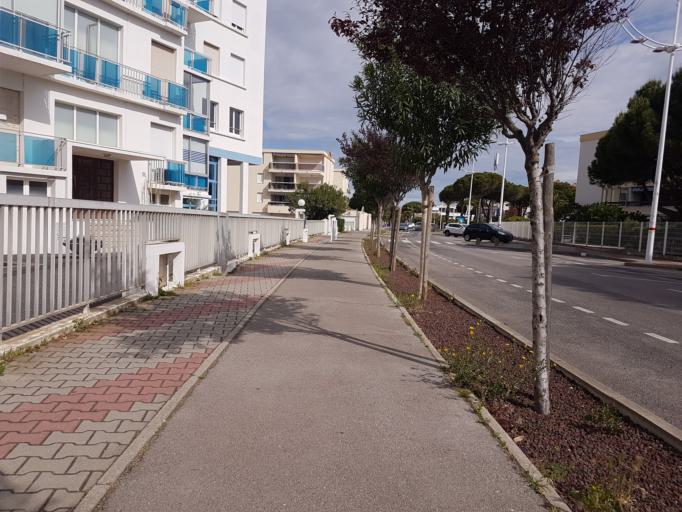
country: FR
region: Languedoc-Roussillon
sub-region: Departement du Gard
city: Le Grau-du-Roi
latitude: 43.5472
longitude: 4.1237
